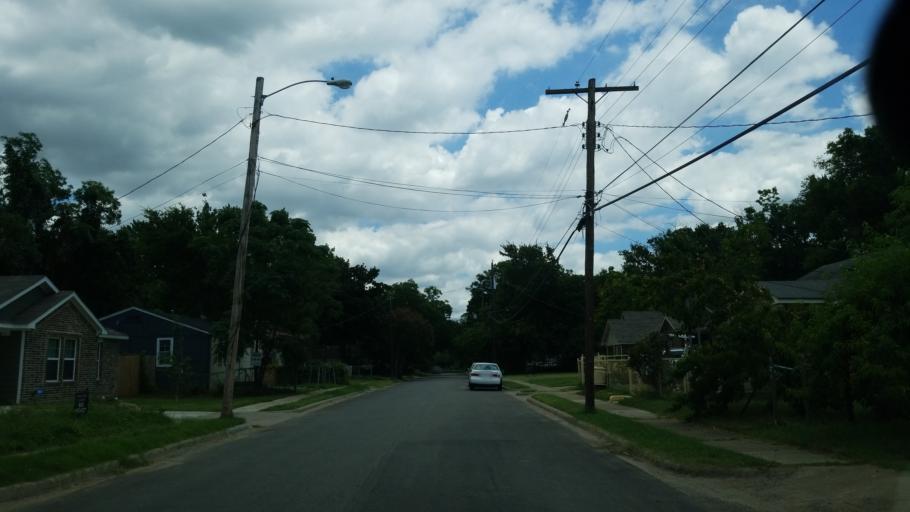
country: US
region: Texas
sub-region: Dallas County
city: Dallas
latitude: 32.7499
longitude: -96.7505
